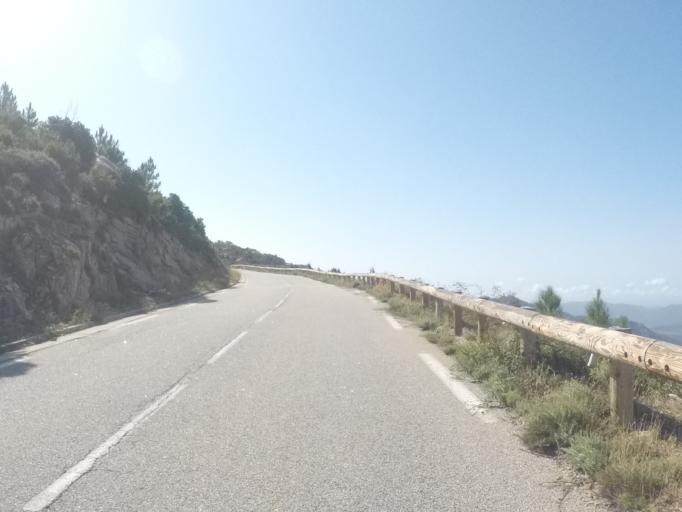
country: FR
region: Corsica
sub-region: Departement de la Corse-du-Sud
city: Olmeto
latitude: 41.7681
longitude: 9.0271
